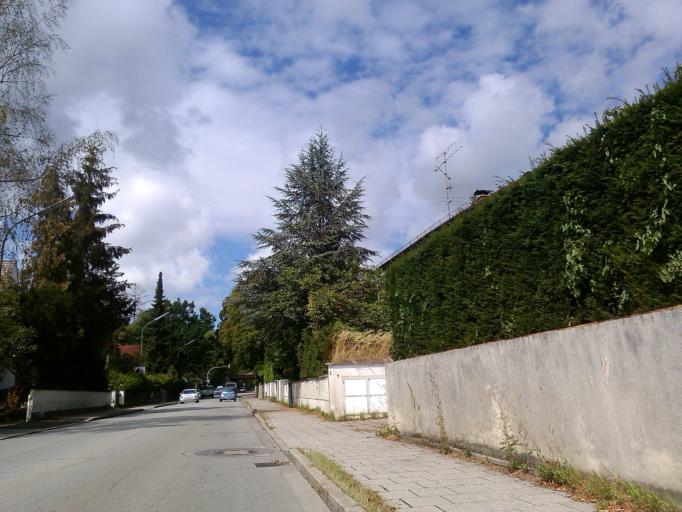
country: DE
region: Bavaria
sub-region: Upper Bavaria
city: Planegg
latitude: 48.1071
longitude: 11.4183
